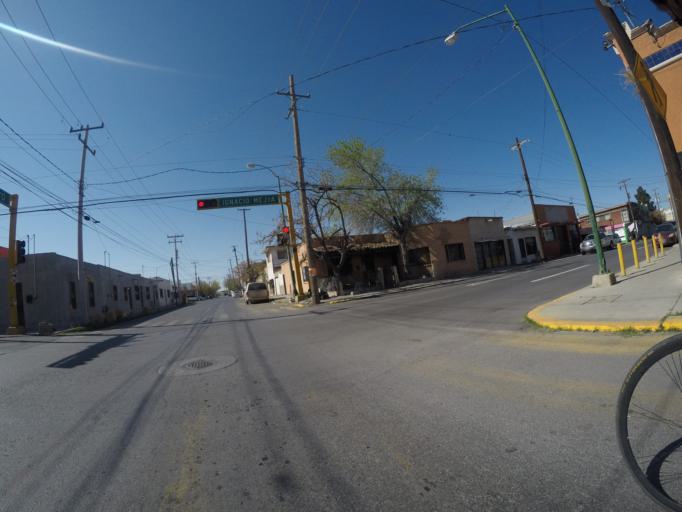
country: MX
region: Chihuahua
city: Ciudad Juarez
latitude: 31.7412
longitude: -106.4738
